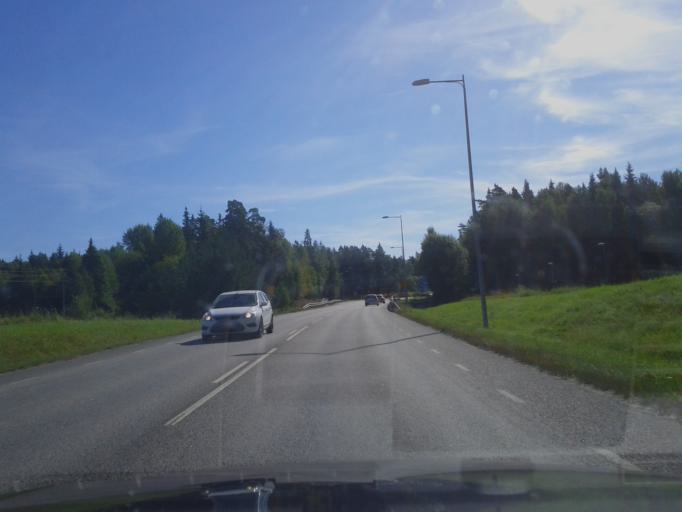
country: SE
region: Stockholm
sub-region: Taby Kommun
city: Taby
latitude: 59.4651
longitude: 18.0673
